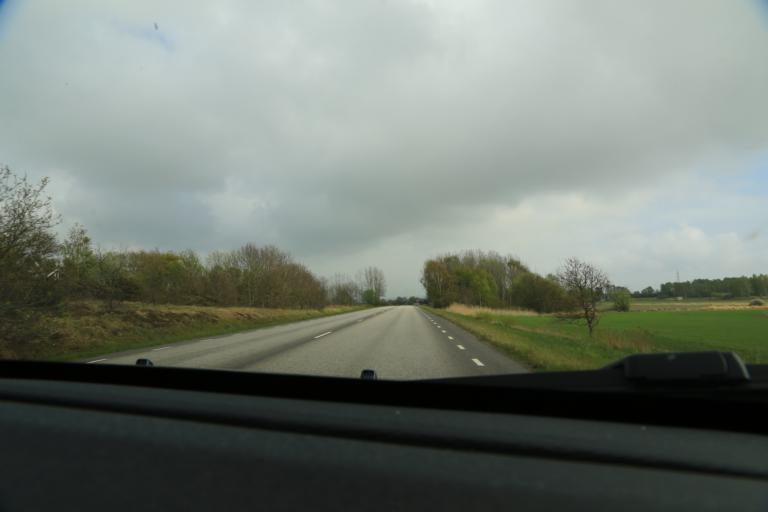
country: SE
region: Halland
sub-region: Kungsbacka Kommun
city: Frillesas
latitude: 57.2379
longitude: 12.1760
